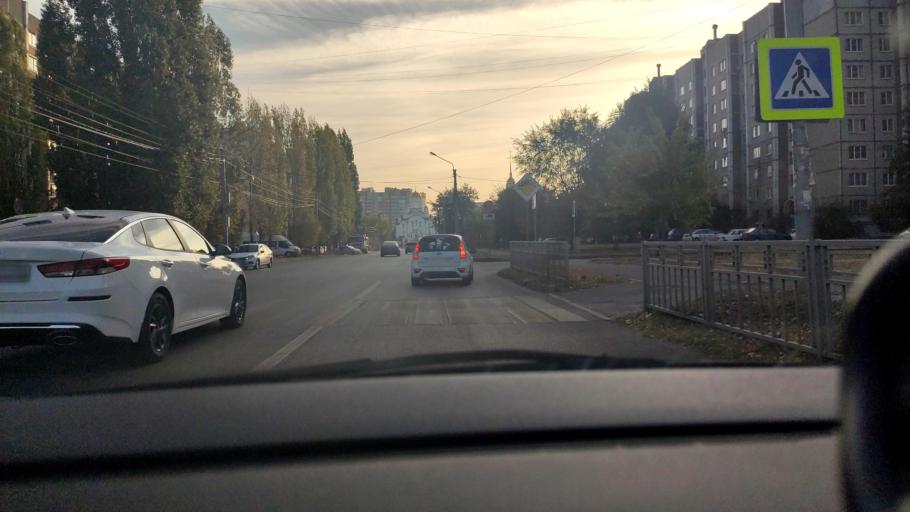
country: RU
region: Voronezj
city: Podgornoye
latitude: 51.7166
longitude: 39.1665
